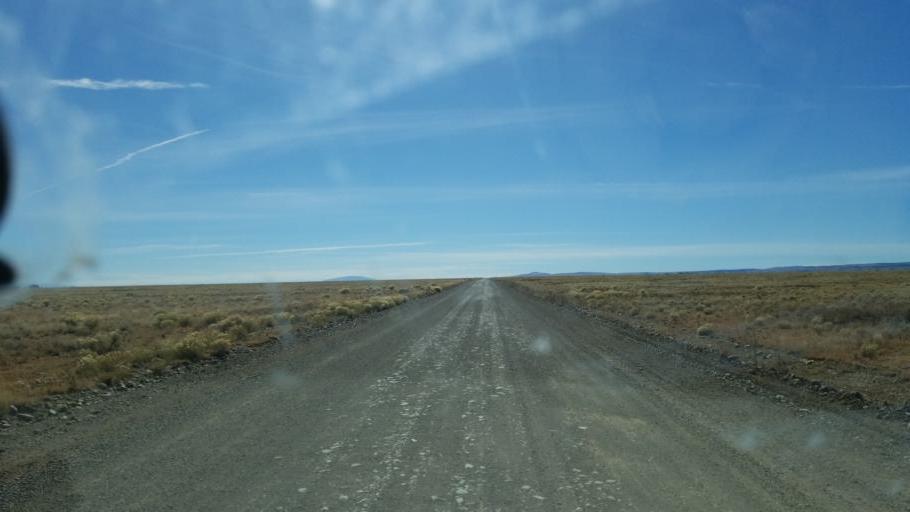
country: US
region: Colorado
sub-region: Rio Grande County
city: Monte Vista
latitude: 37.3723
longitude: -106.1493
